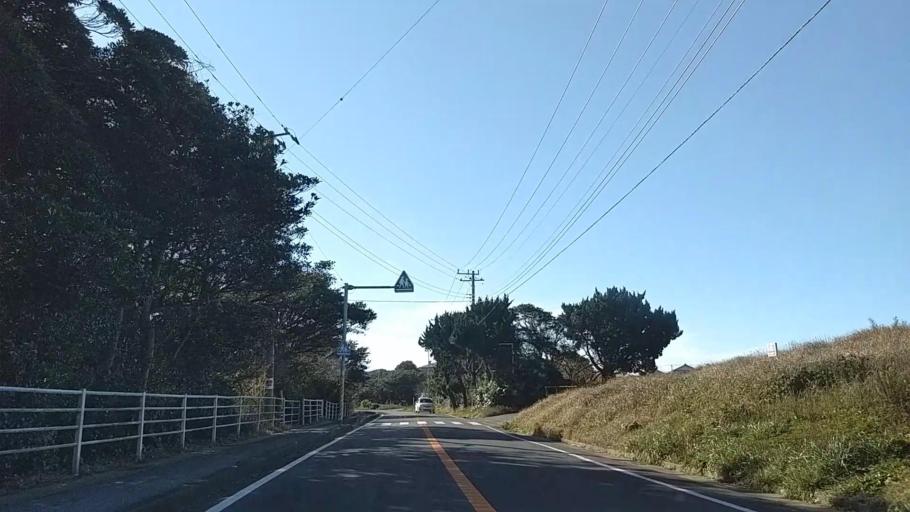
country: JP
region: Chiba
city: Hasaki
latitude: 35.7001
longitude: 140.8617
